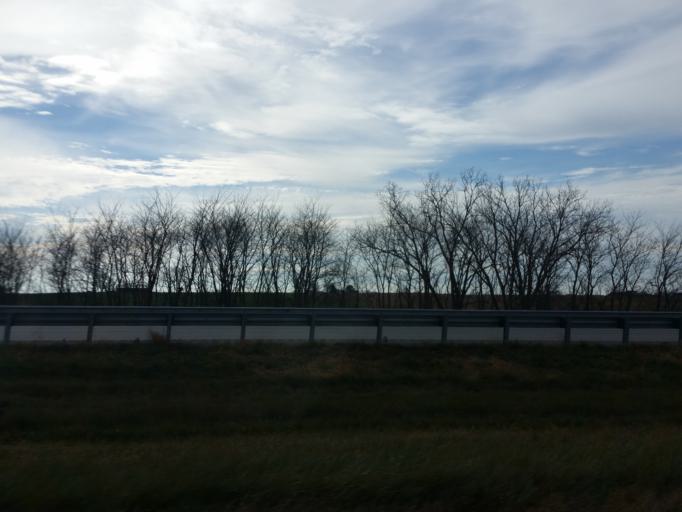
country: US
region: Illinois
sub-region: Henry County
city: Green Rock
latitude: 41.4410
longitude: -90.3540
